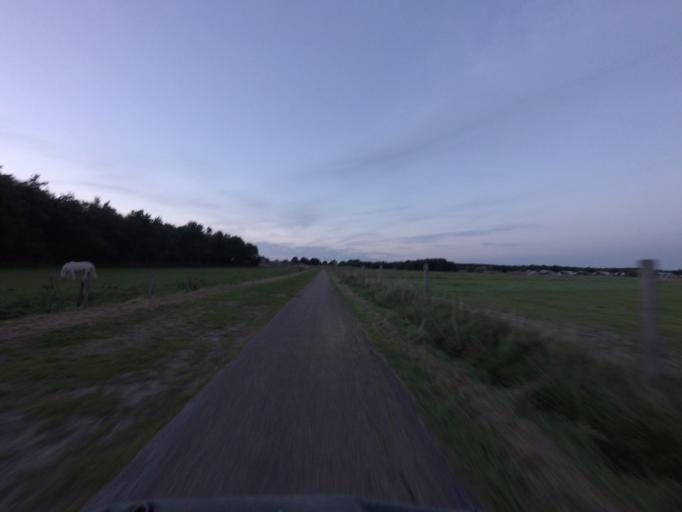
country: NL
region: Friesland
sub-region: Gemeente Ameland
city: Nes
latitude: 53.4529
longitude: 5.7961
